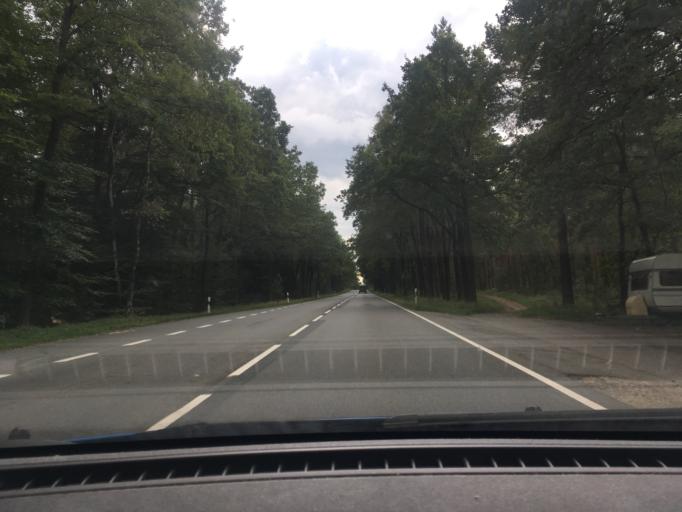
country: DE
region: Lower Saxony
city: Suderburg
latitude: 52.8711
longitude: 10.4944
